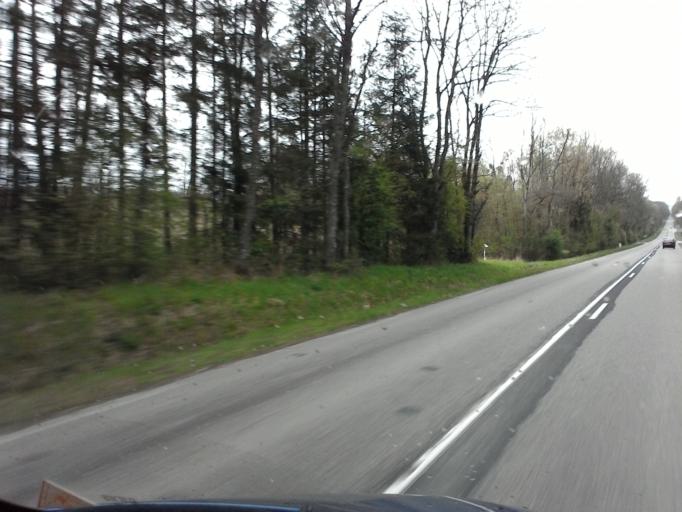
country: FR
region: Lorraine
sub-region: Departement de Meurthe-et-Moselle
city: Domgermain
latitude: 48.6442
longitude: 5.8661
